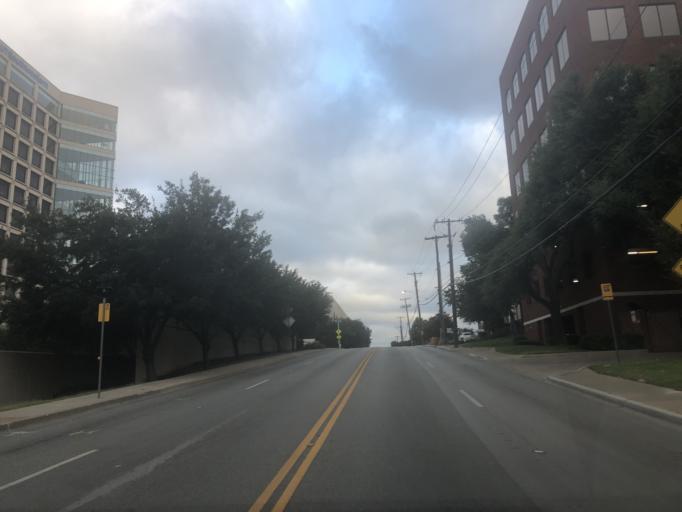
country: US
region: Texas
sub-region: Dallas County
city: University Park
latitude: 32.8204
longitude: -96.8413
